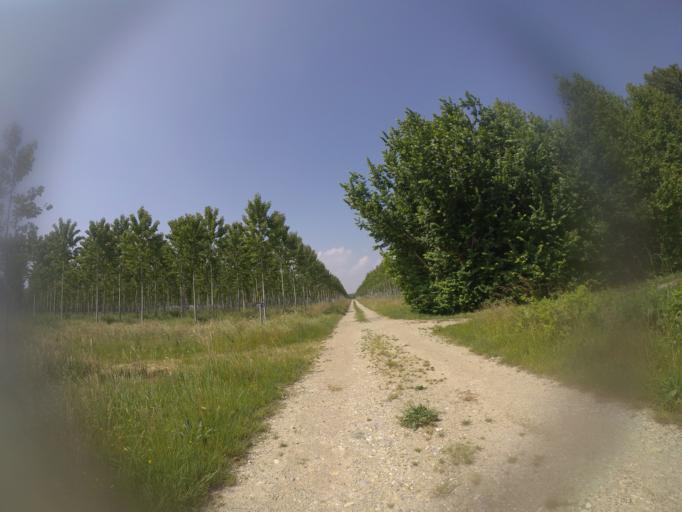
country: IT
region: Friuli Venezia Giulia
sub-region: Provincia di Udine
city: Bertiolo
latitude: 45.9288
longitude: 13.0262
